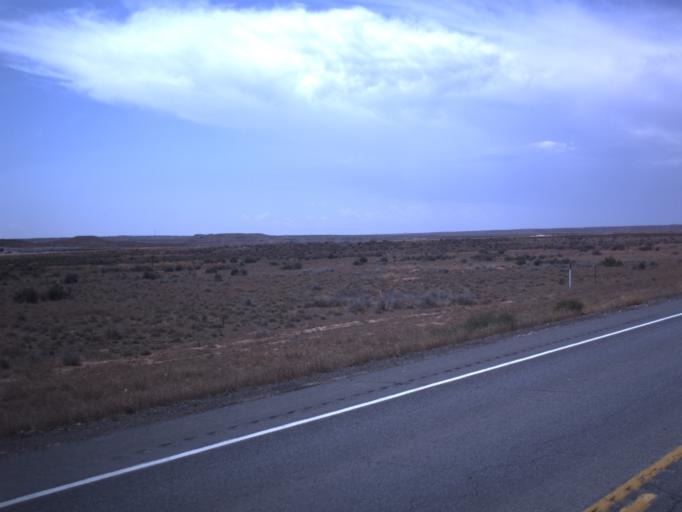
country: US
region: Utah
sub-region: Uintah County
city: Maeser
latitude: 40.3342
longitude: -109.6453
